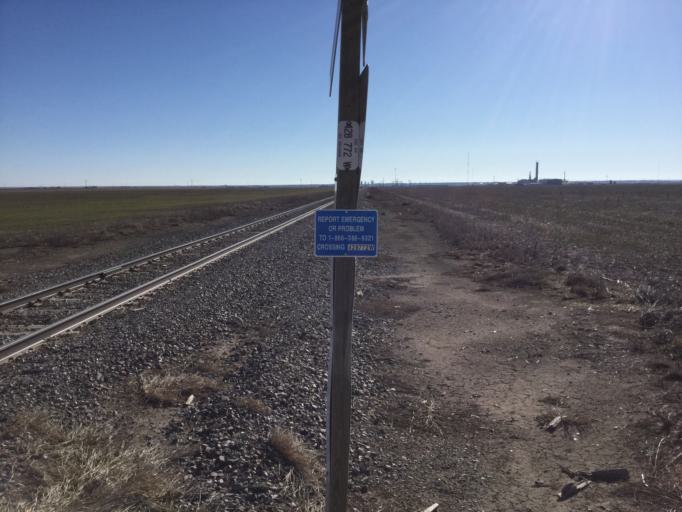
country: US
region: Kansas
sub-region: Scott County
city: Scott City
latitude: 38.4869
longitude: -100.9992
